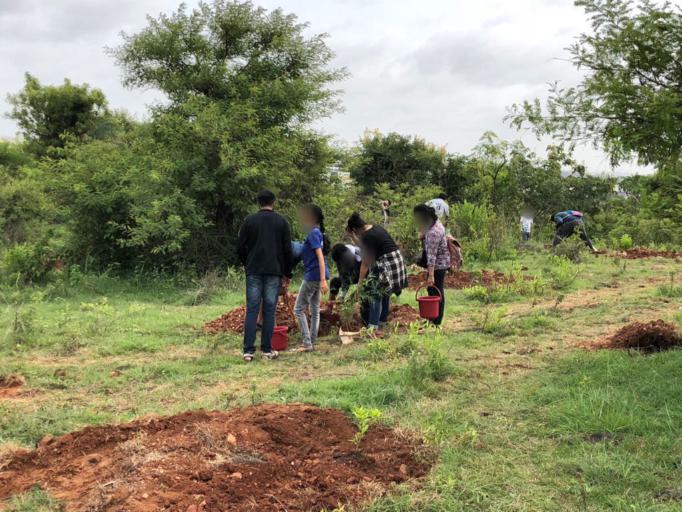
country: IN
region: Karnataka
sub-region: Bangalore Urban
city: Bangalore
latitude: 12.9108
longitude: 77.5027
